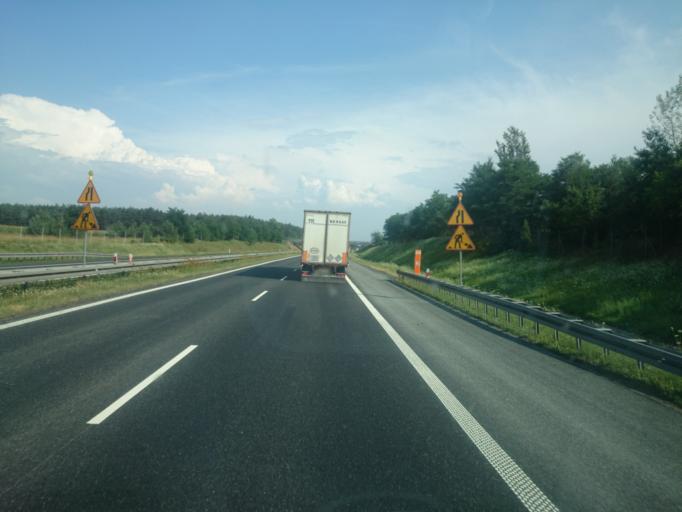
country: PL
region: Opole Voivodeship
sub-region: Powiat opolski
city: Dabrowa
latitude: 50.6548
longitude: 17.7152
